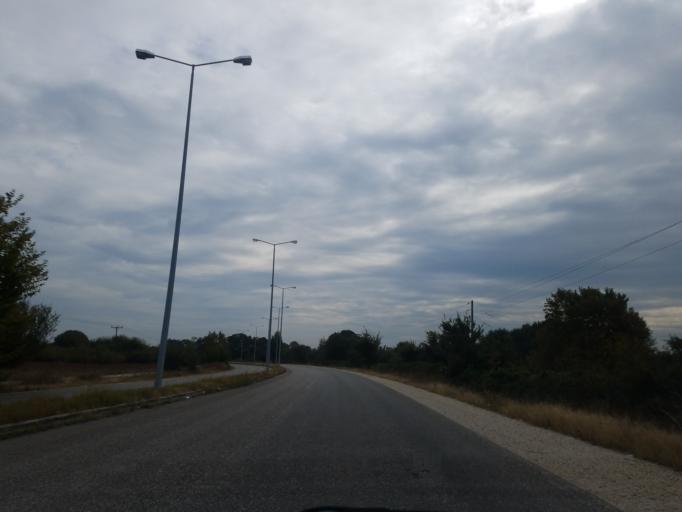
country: GR
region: Thessaly
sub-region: Trikala
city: Megala Kalyvia
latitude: 39.5189
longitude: 21.7623
